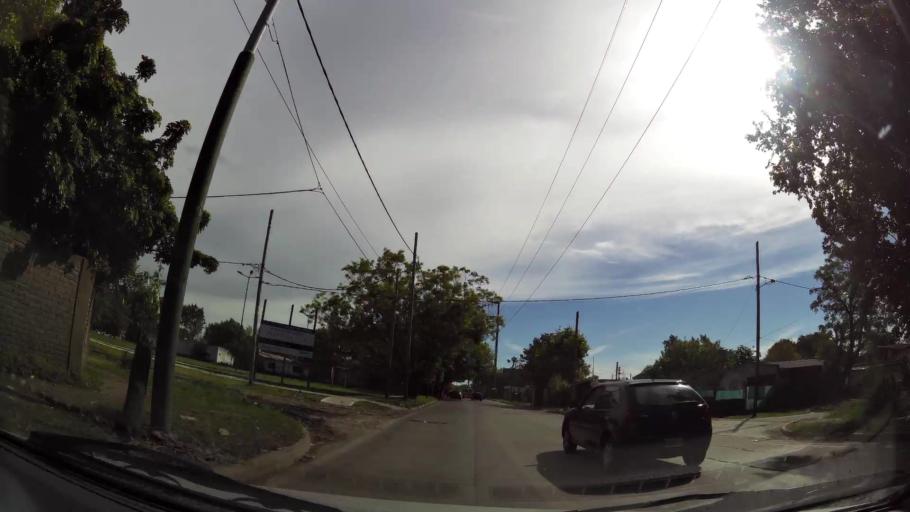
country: AR
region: Buenos Aires
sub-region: Partido de Almirante Brown
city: Adrogue
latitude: -34.8120
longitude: -58.3493
